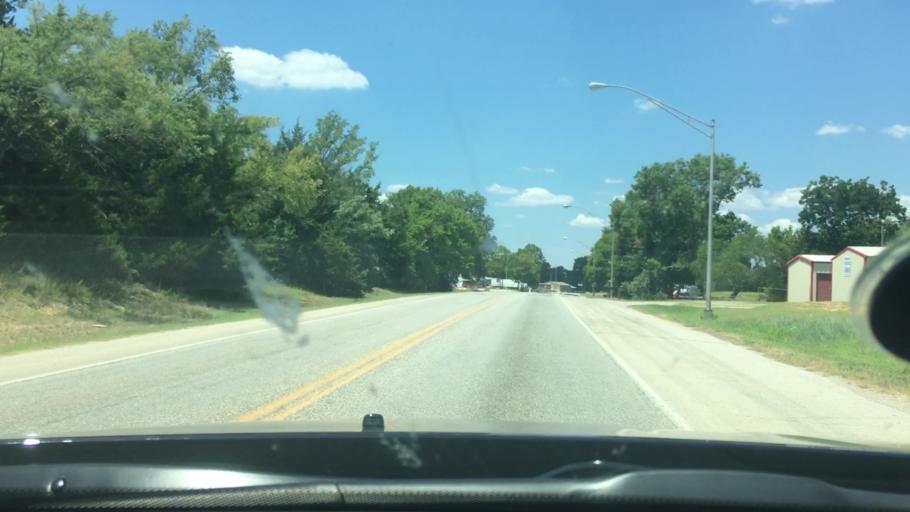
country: US
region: Oklahoma
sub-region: Carter County
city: Dickson
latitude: 34.1863
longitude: -96.8882
